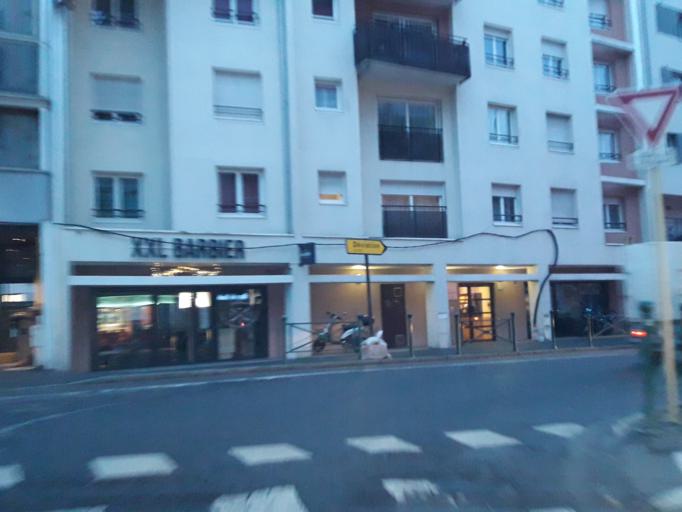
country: FR
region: Rhone-Alpes
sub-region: Departement de la Haute-Savoie
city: Annemasse
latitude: 46.1931
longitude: 6.2328
